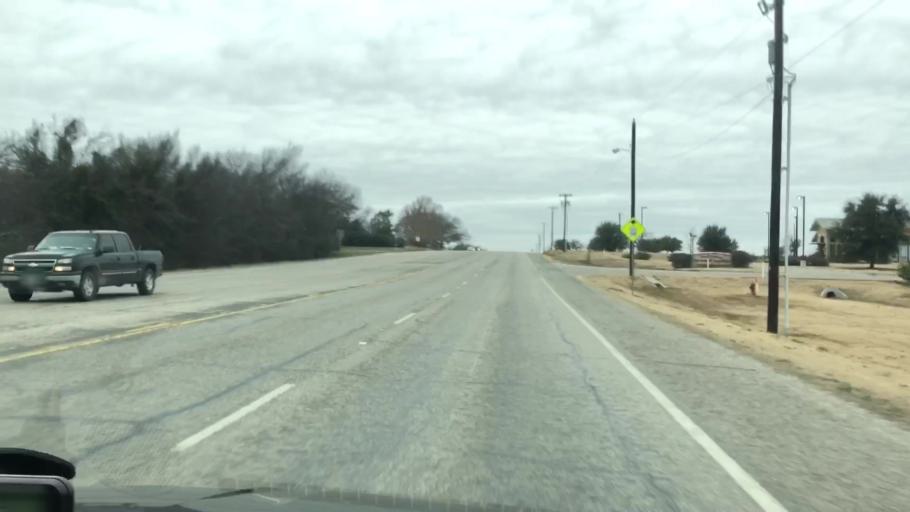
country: US
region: Texas
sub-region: Jack County
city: Jacksboro
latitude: 33.2276
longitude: -98.1659
